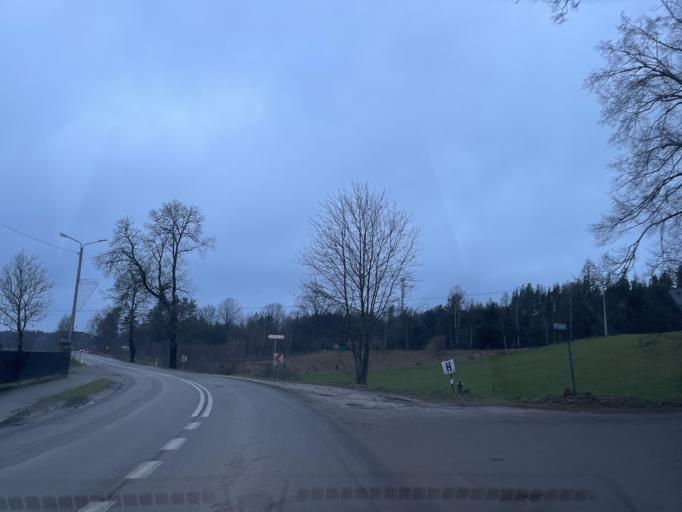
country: PL
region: Pomeranian Voivodeship
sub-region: Powiat wejherowski
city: Szemud
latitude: 54.4161
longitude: 18.1978
